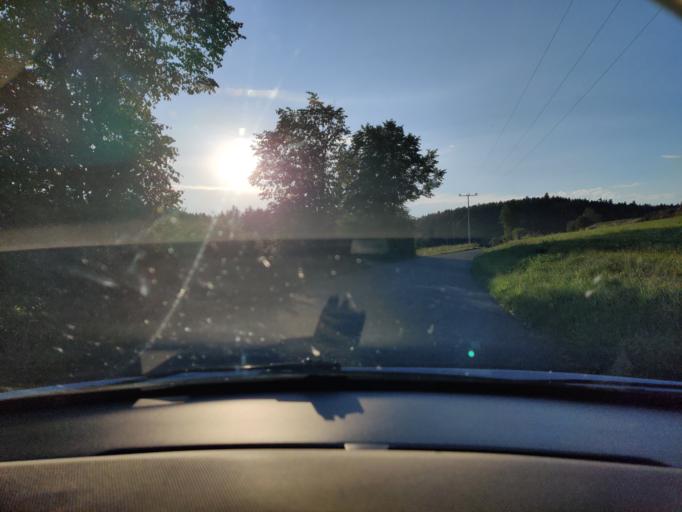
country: DE
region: Bavaria
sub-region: Upper Palatinate
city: Nabburg
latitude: 49.4558
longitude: 12.1682
